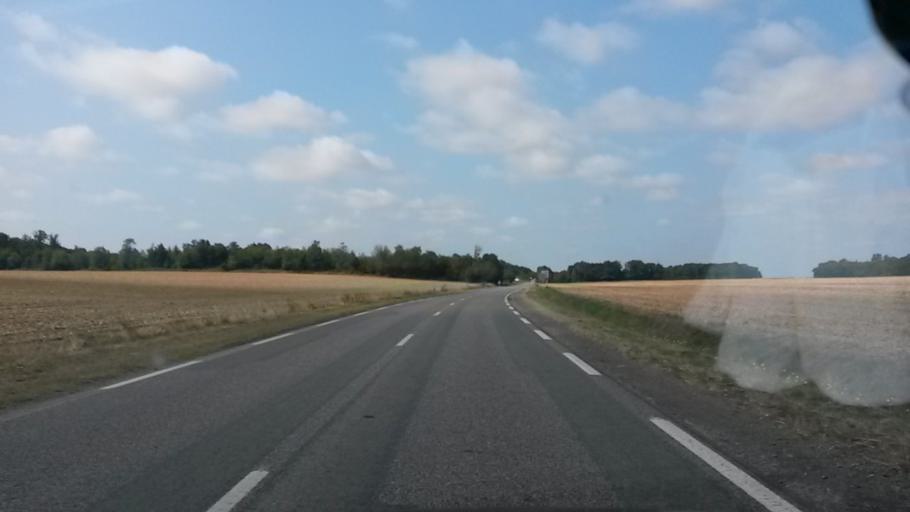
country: FR
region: Haute-Normandie
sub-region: Departement de l'Eure
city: Damville
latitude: 48.8285
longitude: 1.0166
